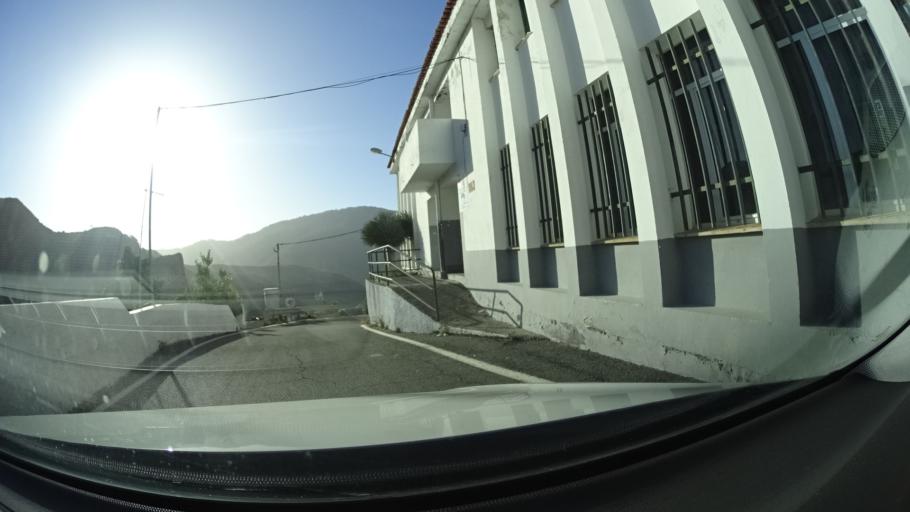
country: ES
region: Canary Islands
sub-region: Provincia de Las Palmas
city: Artenara
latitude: 28.0438
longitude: -15.6526
